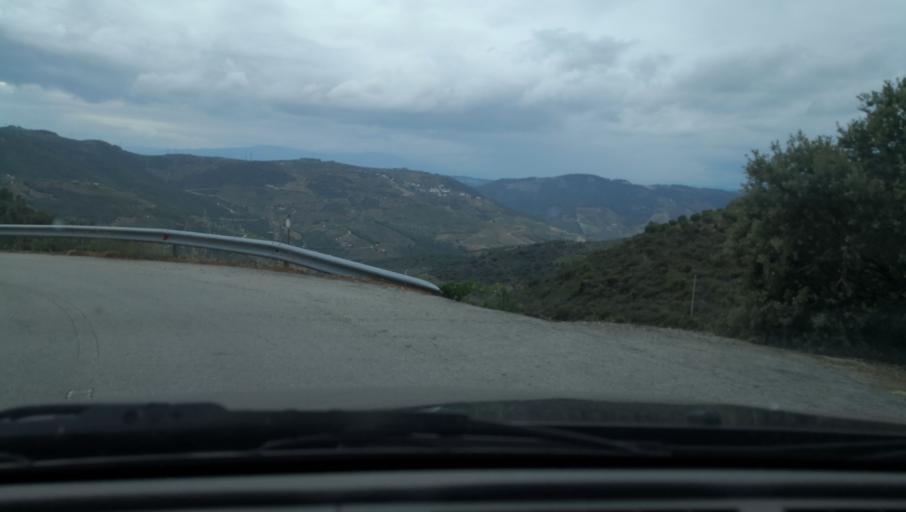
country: PT
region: Viseu
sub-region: Tabuaco
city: Tabuaco
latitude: 41.1264
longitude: -7.6112
